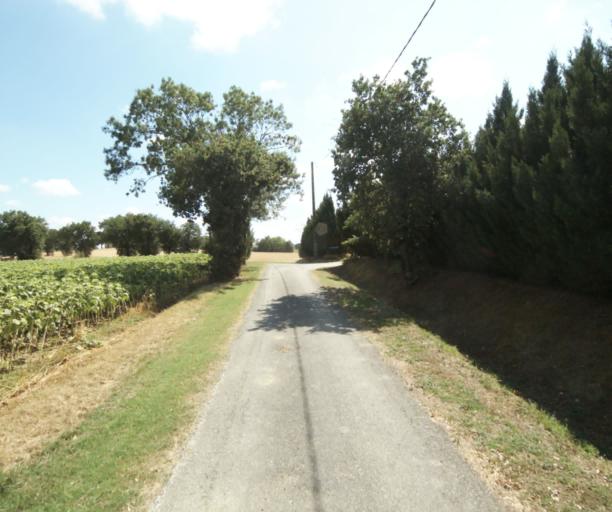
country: FR
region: Midi-Pyrenees
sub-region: Departement de la Haute-Garonne
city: Auriac-sur-Vendinelle
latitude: 43.4613
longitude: 1.8096
